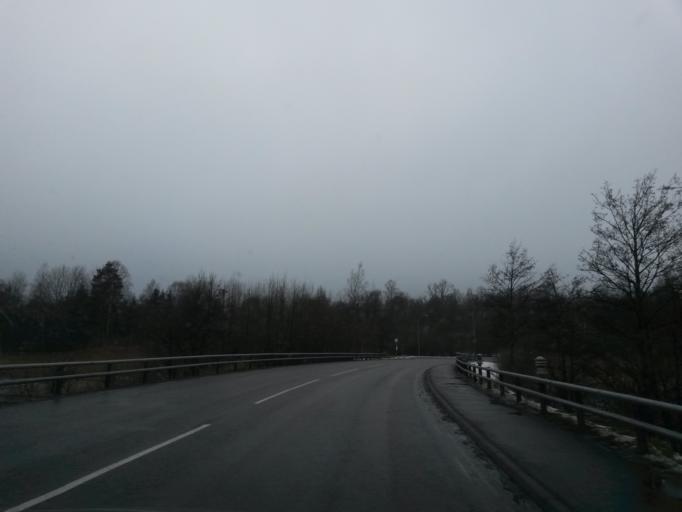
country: SE
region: Vaestra Goetaland
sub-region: Tranemo Kommun
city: Langhem
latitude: 57.6763
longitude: 13.3254
